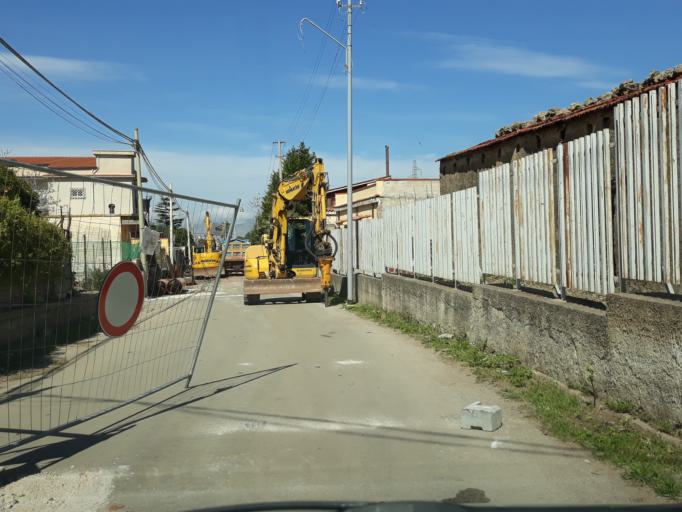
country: IT
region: Sicily
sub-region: Palermo
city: Villa Ciambra
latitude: 38.0795
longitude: 13.3470
